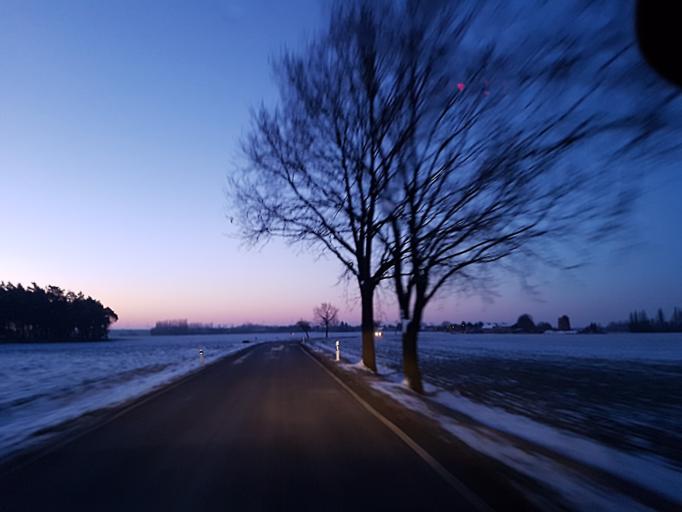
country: DE
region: Brandenburg
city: Falkenberg
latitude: 51.5257
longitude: 13.2995
